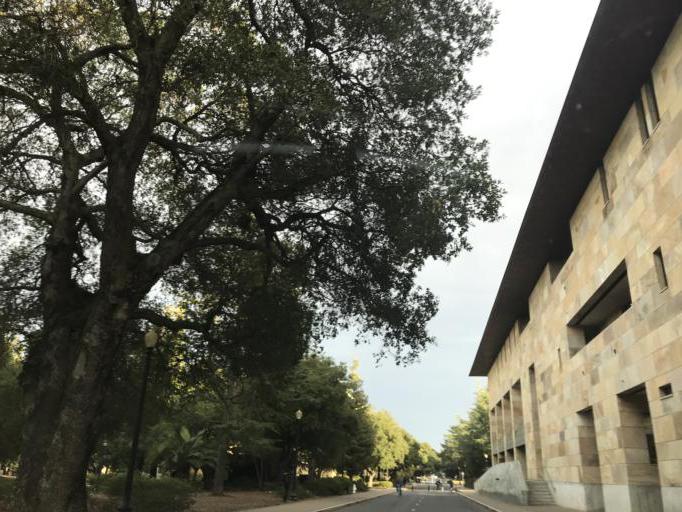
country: US
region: California
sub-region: Santa Clara County
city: Stanford
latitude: 37.4301
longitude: -122.1751
